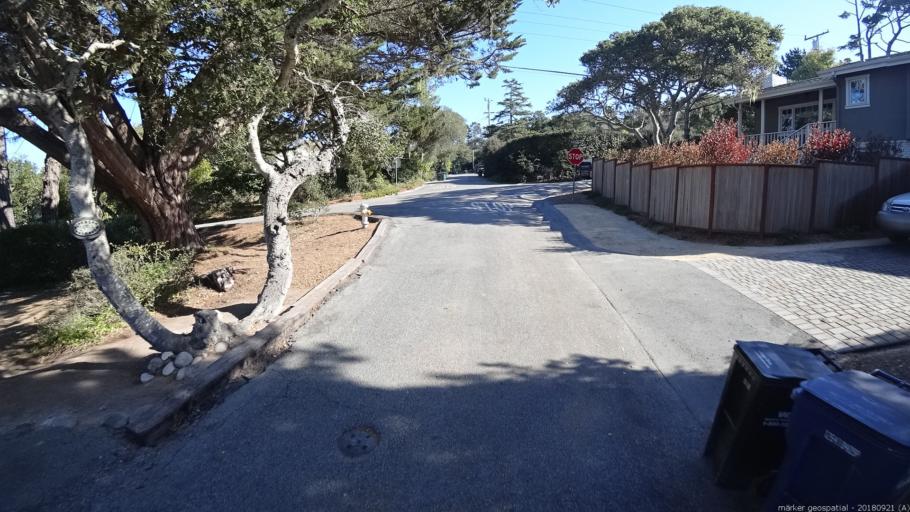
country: US
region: California
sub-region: Monterey County
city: Carmel-by-the-Sea
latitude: 36.5669
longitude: -121.9194
